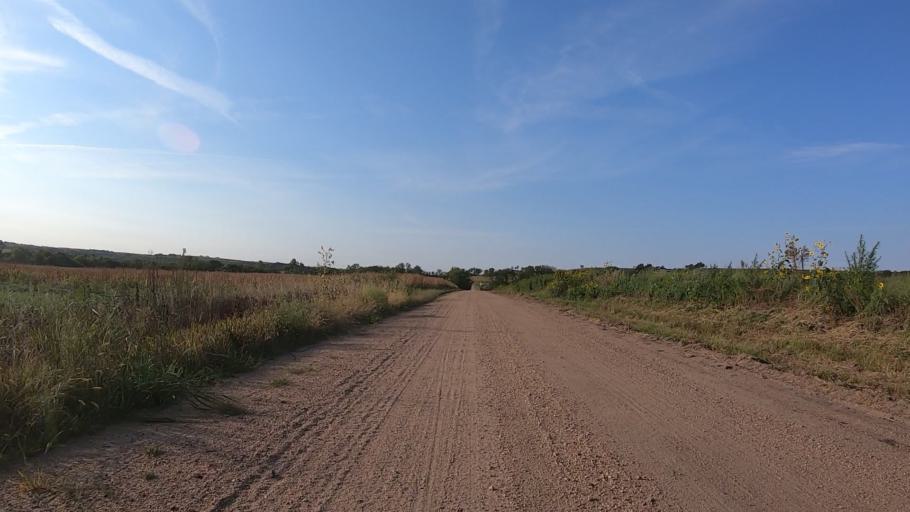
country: US
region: Kansas
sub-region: Marshall County
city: Blue Rapids
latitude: 39.6938
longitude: -96.7792
